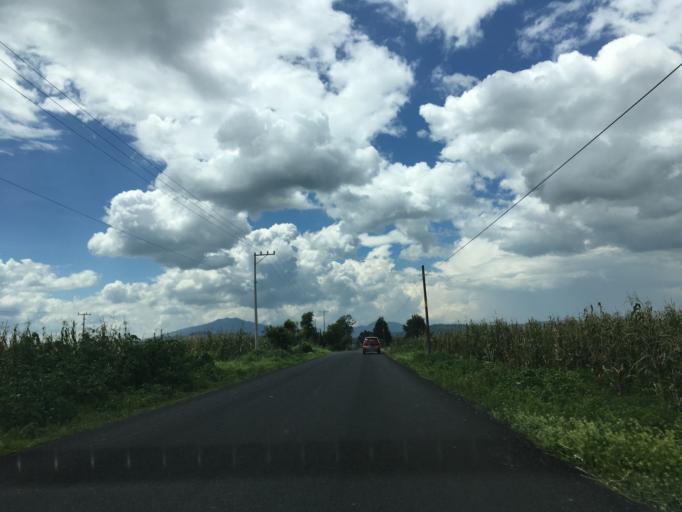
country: MX
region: Michoacan
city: Zacapu
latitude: 19.8371
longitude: -101.7369
